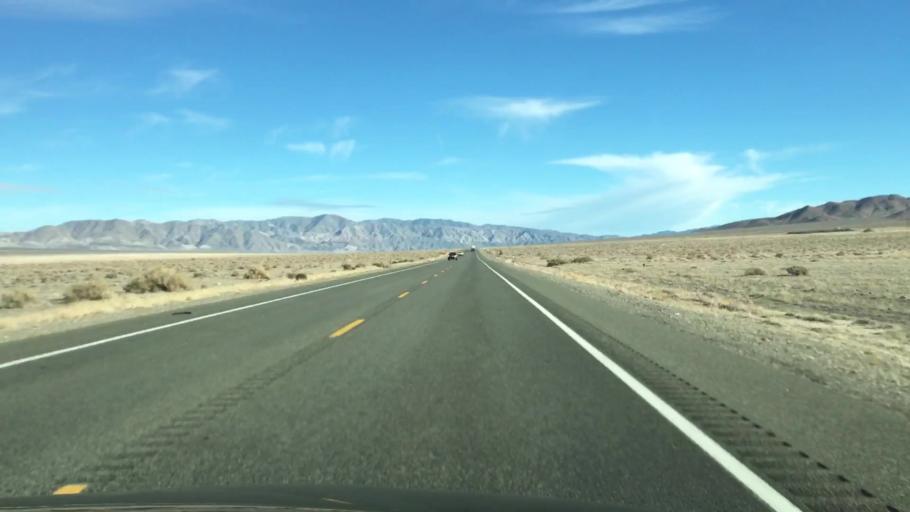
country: US
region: Nevada
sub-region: Mineral County
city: Hawthorne
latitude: 38.5372
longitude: -118.3374
